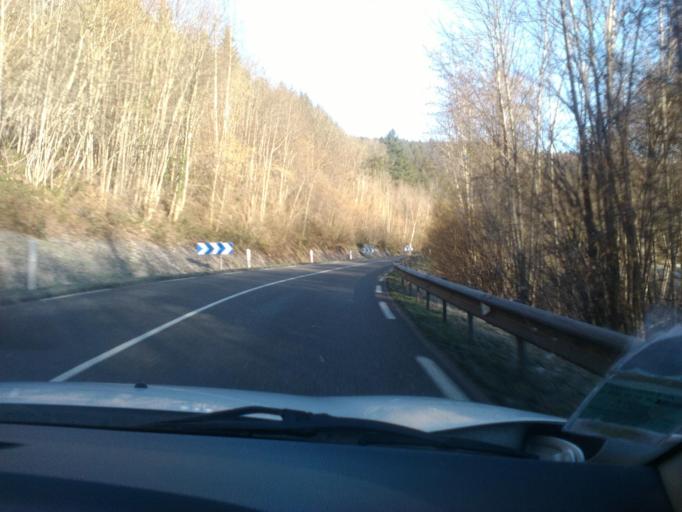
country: FR
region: Alsace
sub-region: Departement du Bas-Rhin
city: Rothau
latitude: 48.4333
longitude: 7.1825
